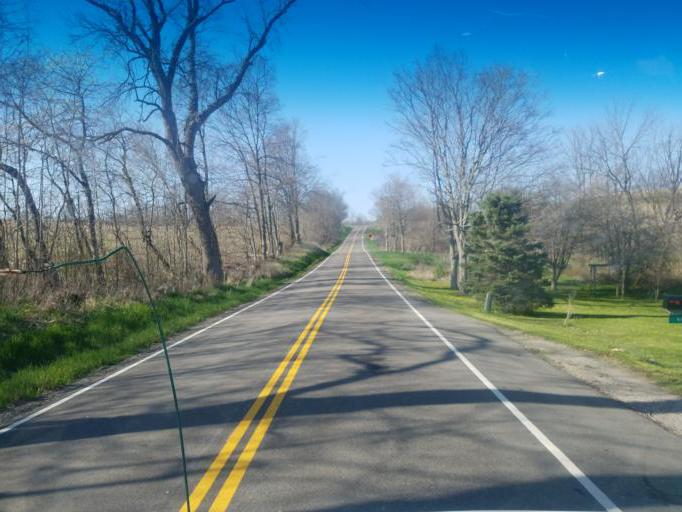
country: US
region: Ohio
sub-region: Muskingum County
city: Frazeysburg
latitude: 40.2698
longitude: -82.1165
